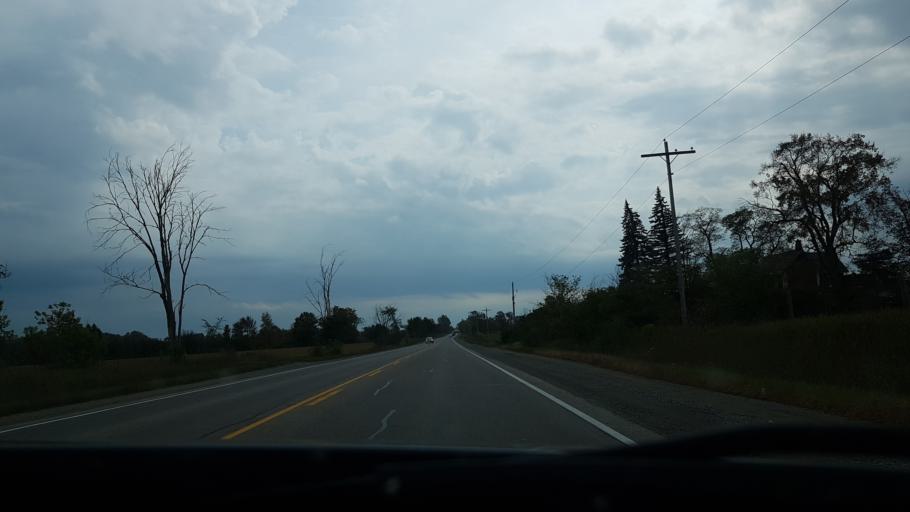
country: CA
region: Ontario
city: Omemee
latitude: 44.4764
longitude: -78.7605
